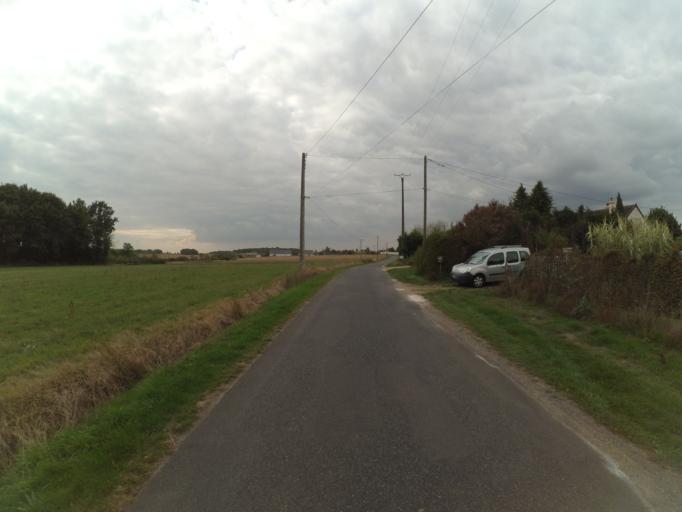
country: FR
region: Centre
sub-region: Departement d'Indre-et-Loire
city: Poce-sur-Cisse
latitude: 47.4991
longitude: 0.9794
